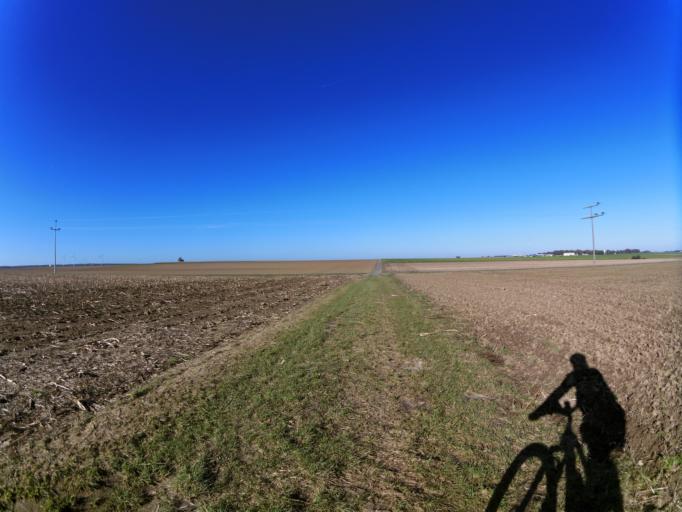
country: DE
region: Bavaria
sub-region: Regierungsbezirk Unterfranken
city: Giebelstadt
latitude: 49.6746
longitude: 9.9336
